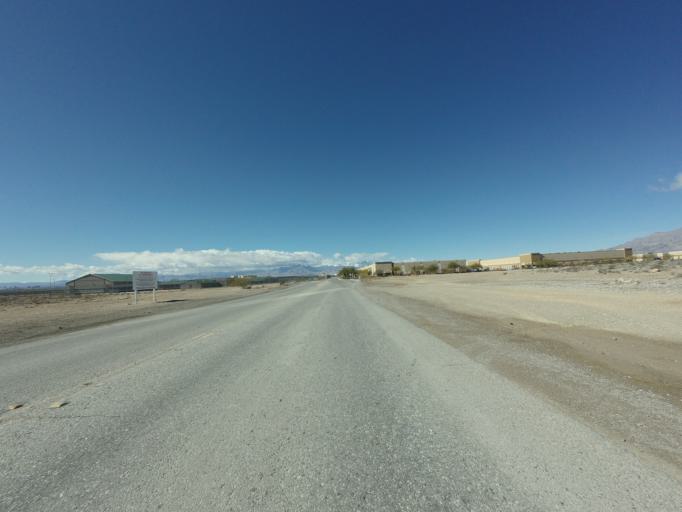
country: US
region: Nevada
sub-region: Clark County
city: Nellis Air Force Base
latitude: 36.2659
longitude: -115.0516
